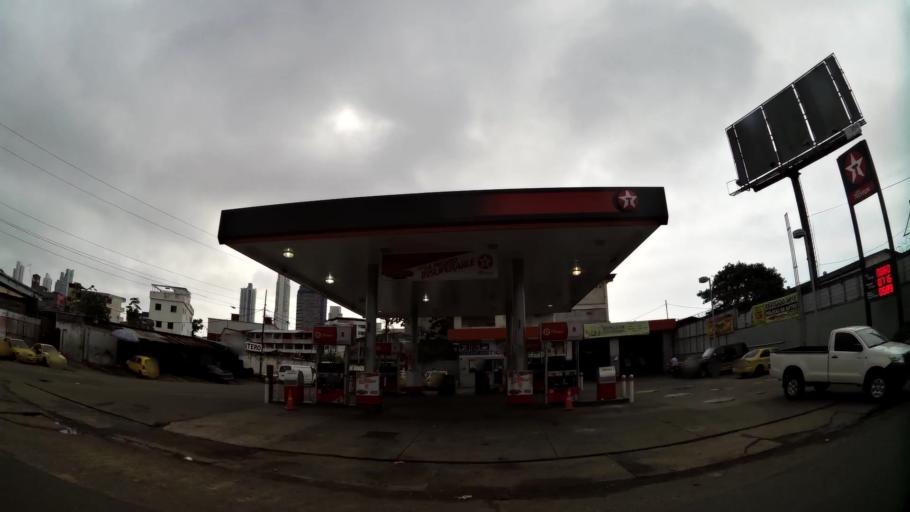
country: PA
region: Panama
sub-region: Distrito de Panama
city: Ancon
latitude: 8.9698
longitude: -79.5411
